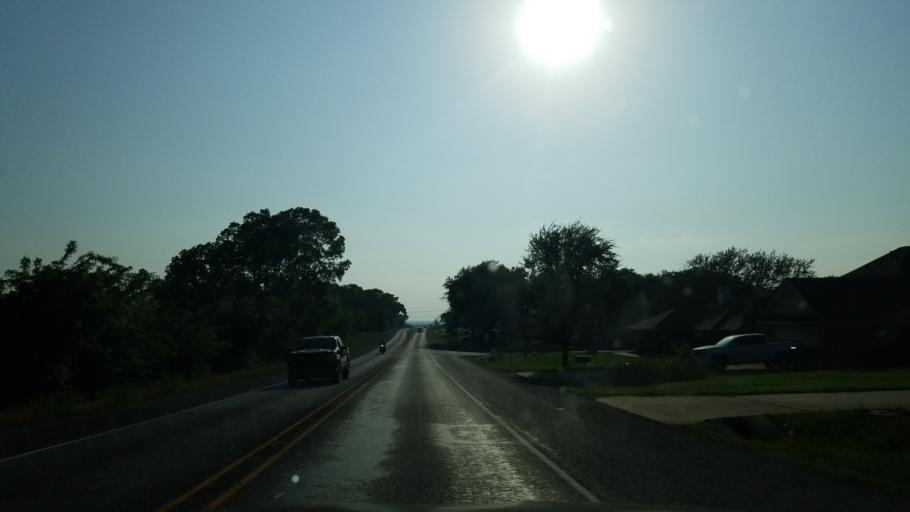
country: US
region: Texas
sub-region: Denton County
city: Aubrey
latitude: 33.3043
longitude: -96.9888
